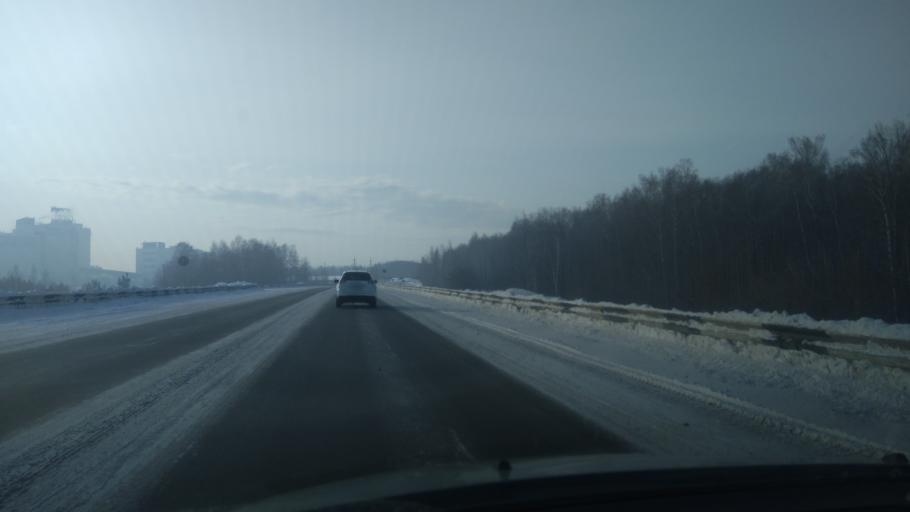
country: RU
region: Sverdlovsk
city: Bogdanovich
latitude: 56.8112
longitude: 62.0409
